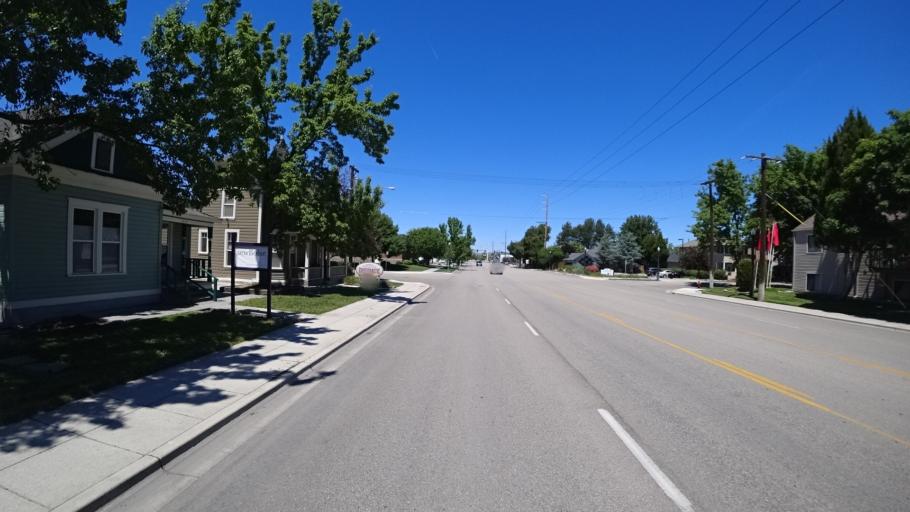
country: US
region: Idaho
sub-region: Ada County
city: Boise
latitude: 43.6157
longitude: -116.2154
